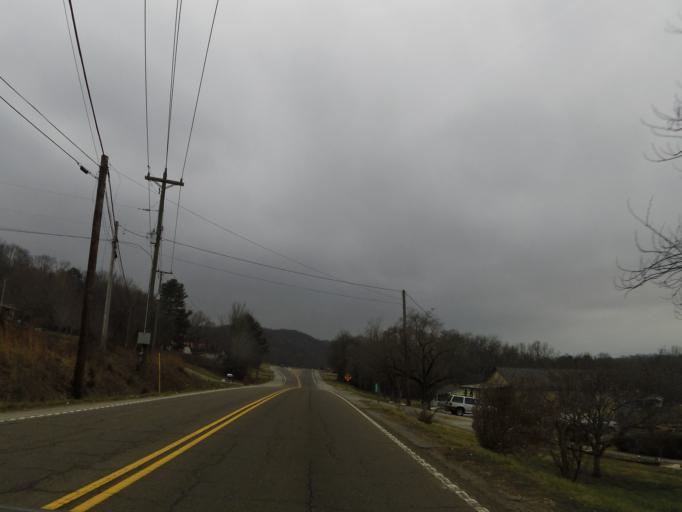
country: US
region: Tennessee
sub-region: Anderson County
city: Rocky Top
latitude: 36.1808
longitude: -84.1436
